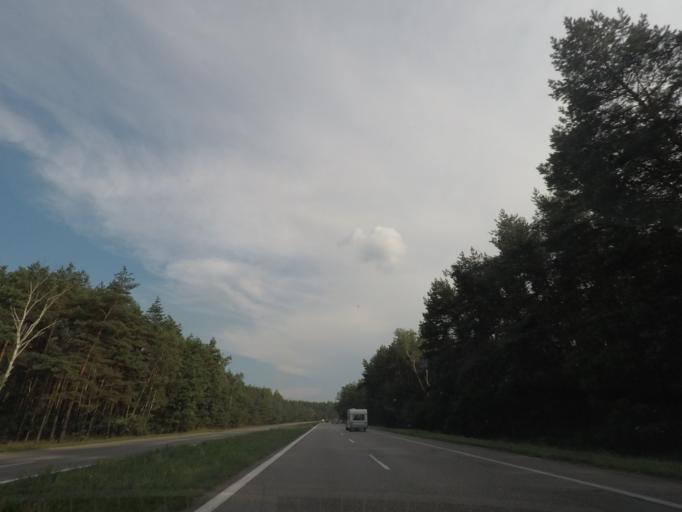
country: PL
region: Silesian Voivodeship
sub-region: Dabrowa Gornicza
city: Dabrowa Gornicza
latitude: 50.3713
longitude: 19.2477
